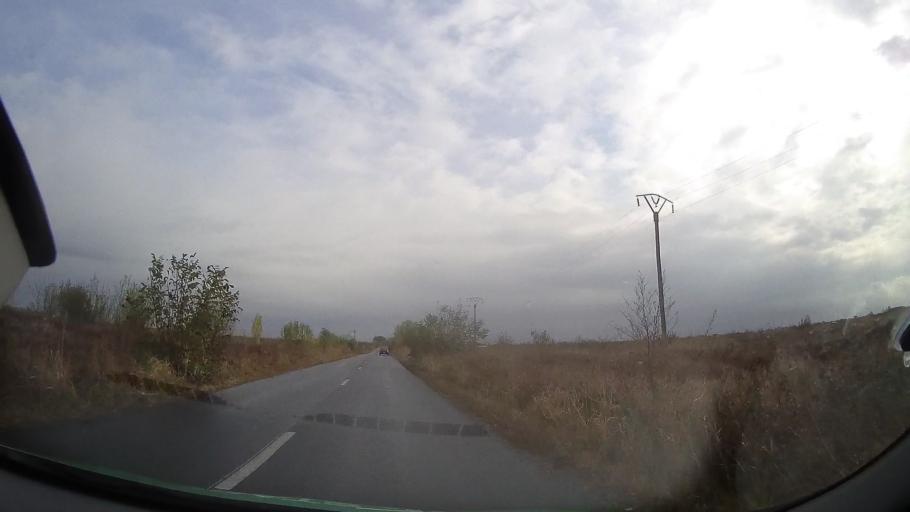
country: RO
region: Ialomita
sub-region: Comuna Maia
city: Maia
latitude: 44.7493
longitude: 26.3927
